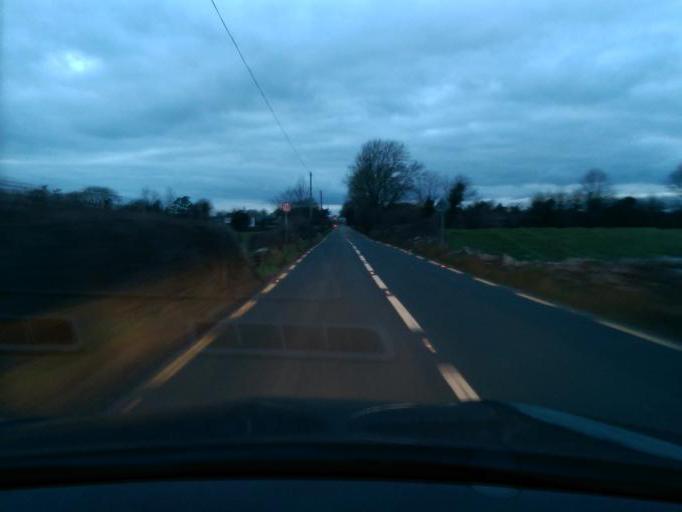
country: IE
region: Connaught
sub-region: County Galway
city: Portumna
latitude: 53.1558
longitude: -8.2692
